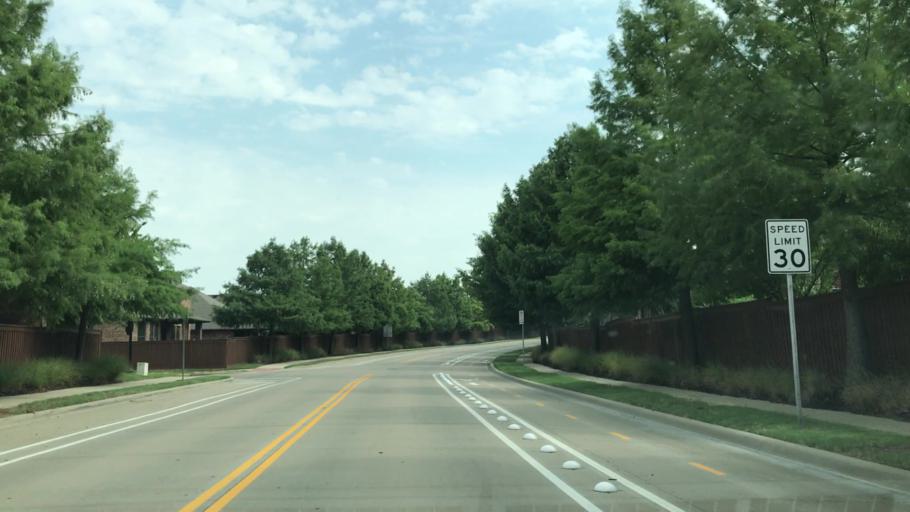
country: US
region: Texas
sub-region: Tarrant County
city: Keller
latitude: 32.9044
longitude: -97.2840
